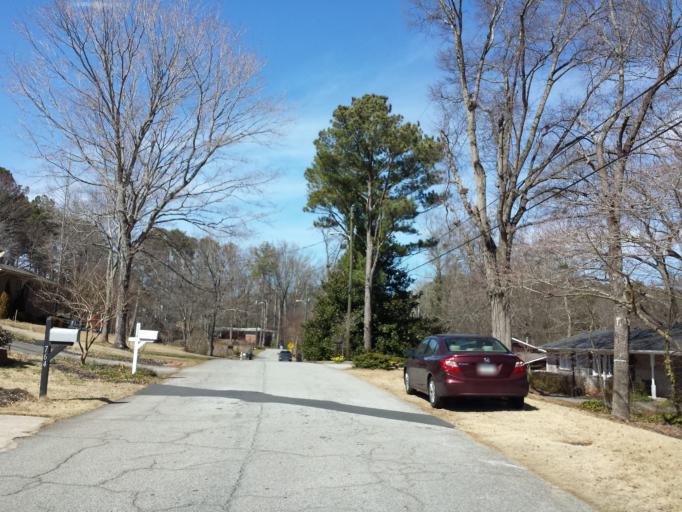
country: US
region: Georgia
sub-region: Cobb County
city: Smyrna
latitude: 33.9333
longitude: -84.4773
